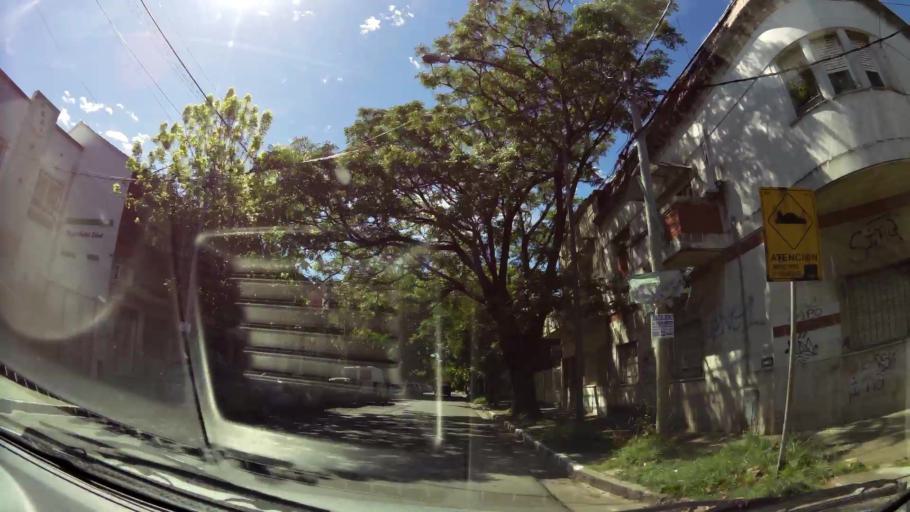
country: AR
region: Buenos Aires
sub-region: Partido de Quilmes
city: Quilmes
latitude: -34.7025
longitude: -58.2948
